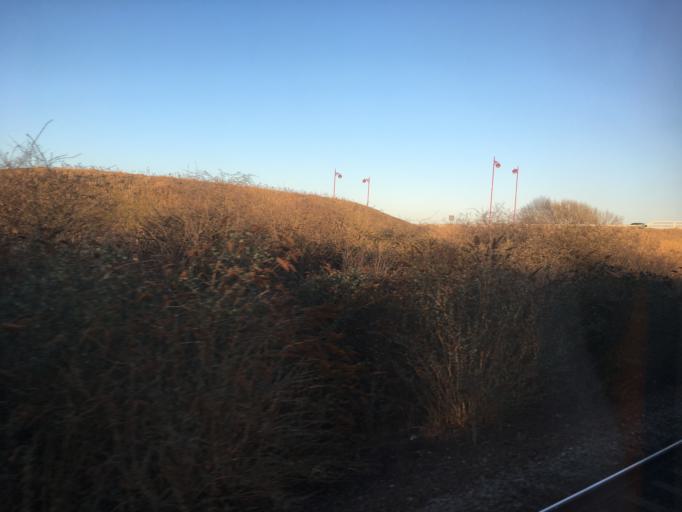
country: GB
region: England
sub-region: Derby
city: Derby
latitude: 52.9091
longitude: -1.4499
